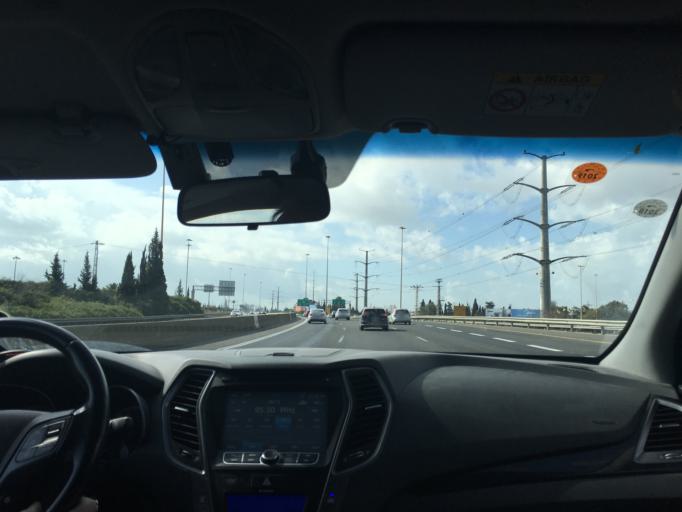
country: IL
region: Tel Aviv
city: Azor
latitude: 32.0124
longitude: 34.8158
